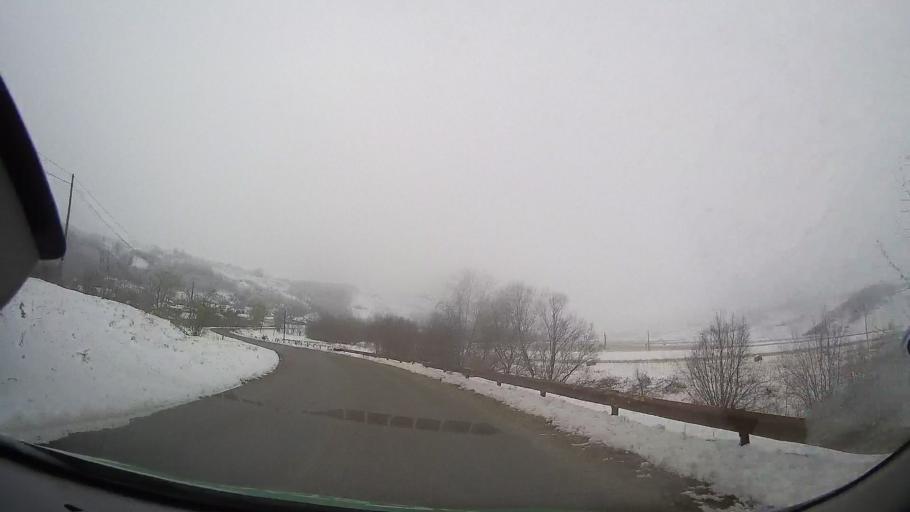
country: RO
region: Bacau
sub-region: Comuna Vultureni
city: Vultureni
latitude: 46.3939
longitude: 27.2778
